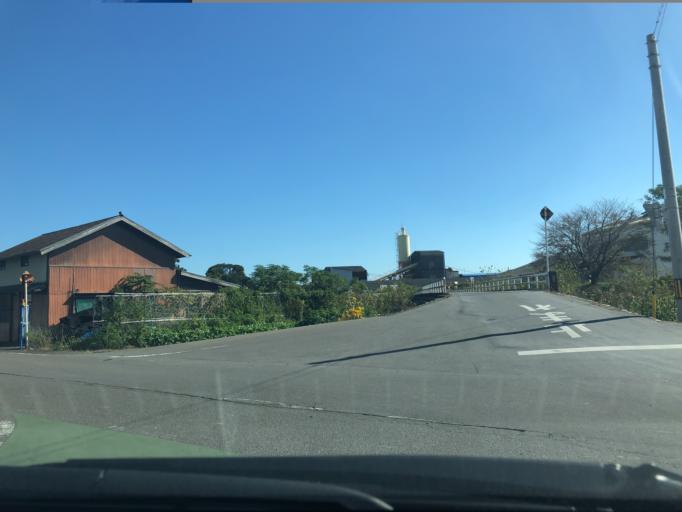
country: JP
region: Gifu
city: Godo
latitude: 35.4058
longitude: 136.6523
